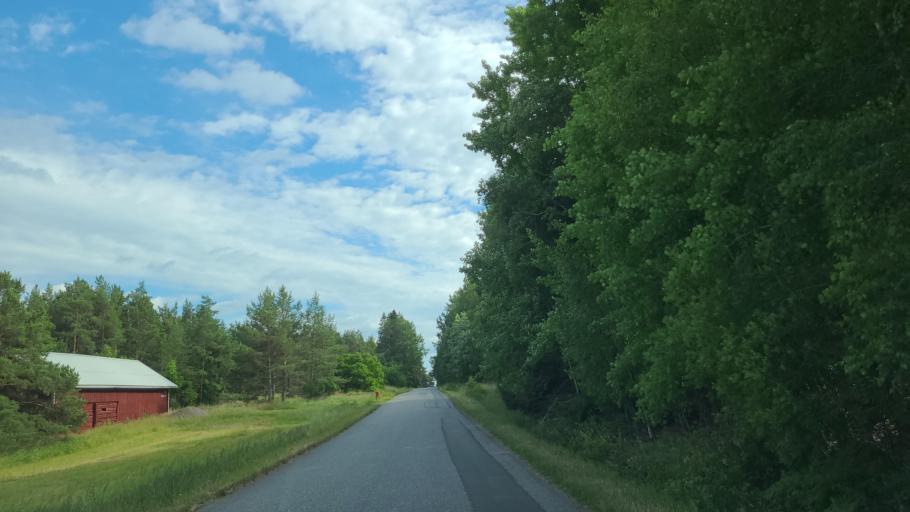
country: FI
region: Varsinais-Suomi
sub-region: Turku
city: Rymaettylae
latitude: 60.3050
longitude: 21.9412
